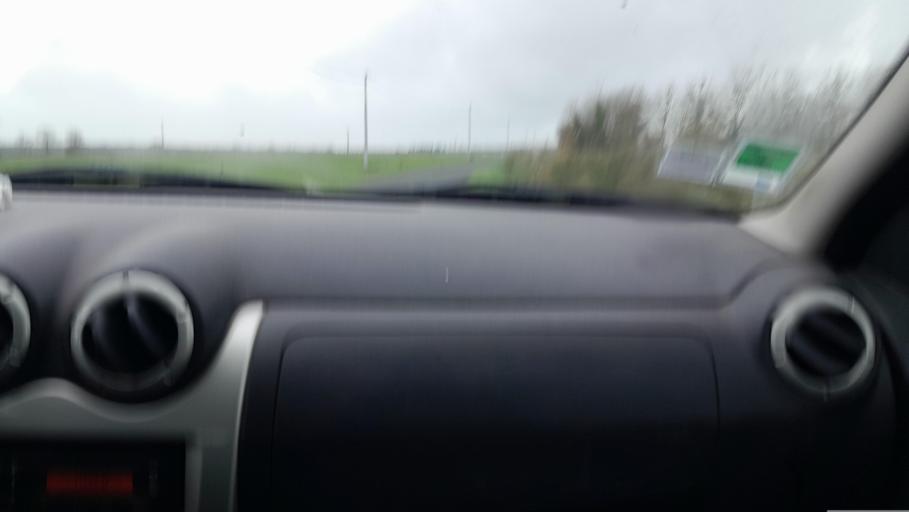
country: FR
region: Brittany
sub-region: Departement d'Ille-et-Vilaine
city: La Guerche-de-Bretagne
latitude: 47.9134
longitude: -1.1523
